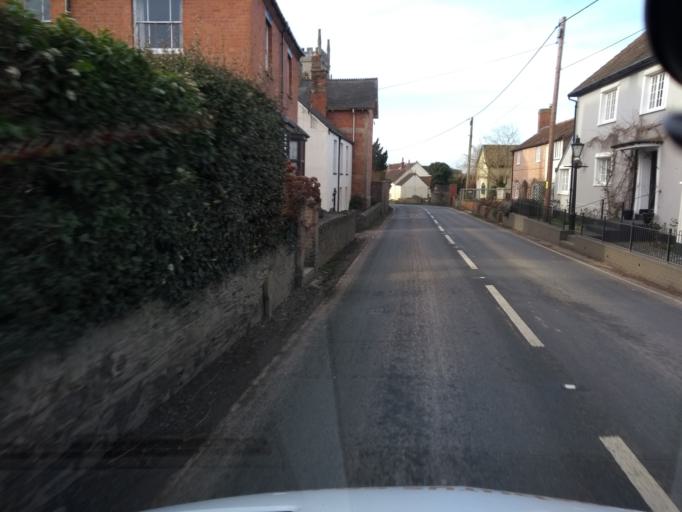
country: GB
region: England
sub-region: Somerset
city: Westonzoyland
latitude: 51.0557
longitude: -2.9526
